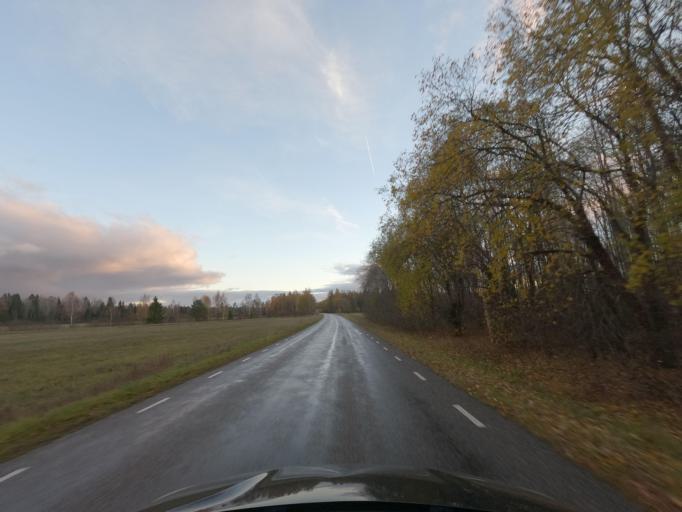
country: EE
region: Raplamaa
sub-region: Kohila vald
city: Kohila
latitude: 59.0878
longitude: 24.6743
